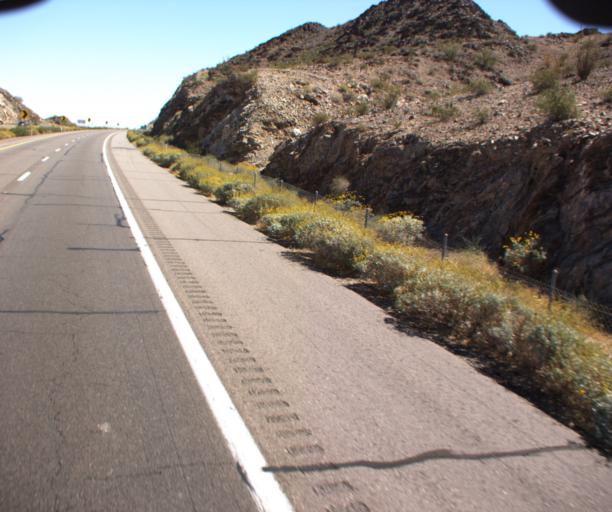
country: US
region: Arizona
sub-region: Yuma County
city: Wellton
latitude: 32.7256
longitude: -113.7502
